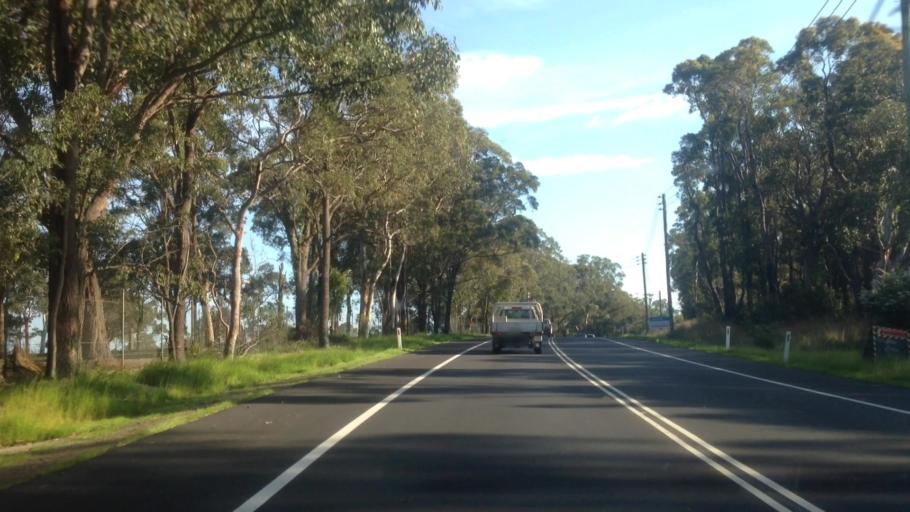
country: AU
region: New South Wales
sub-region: Lake Macquarie Shire
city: Dora Creek
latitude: -33.1174
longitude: 151.4783
